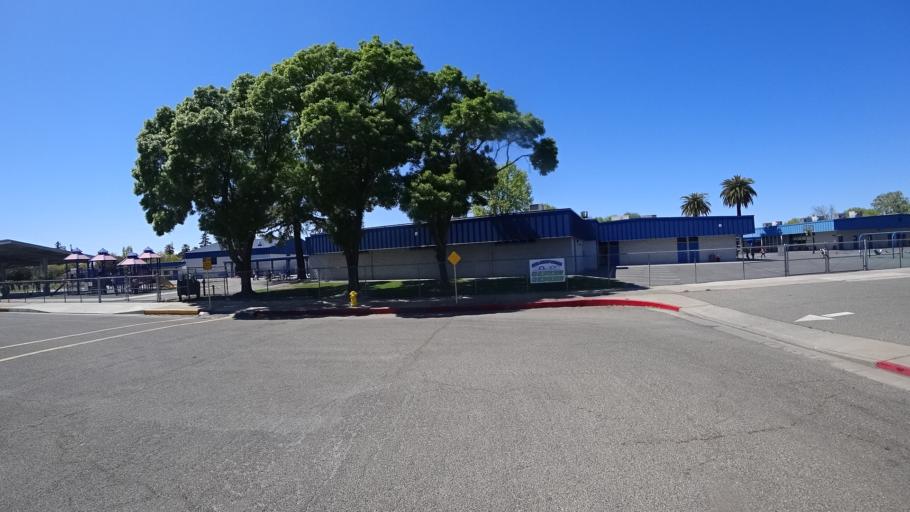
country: US
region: California
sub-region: Glenn County
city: Orland
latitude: 39.7452
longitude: -122.1901
